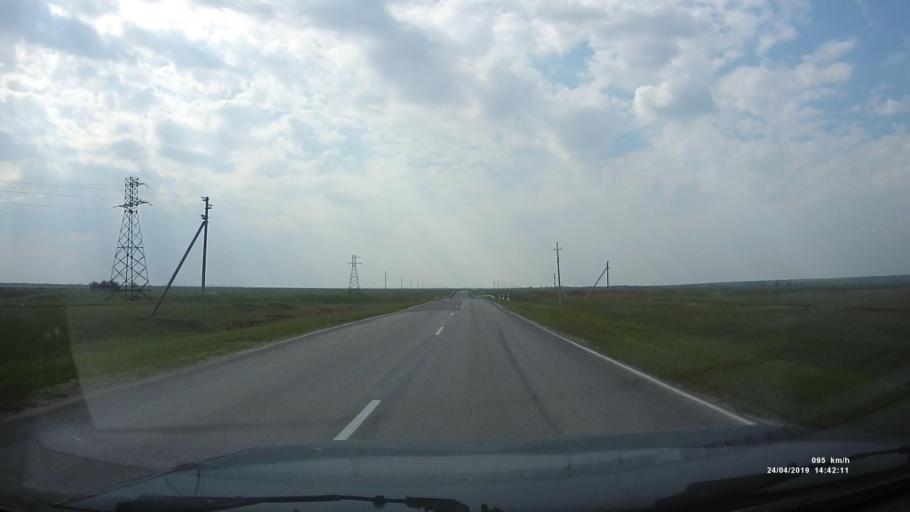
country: RU
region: Rostov
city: Remontnoye
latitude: 46.4508
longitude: 43.8670
